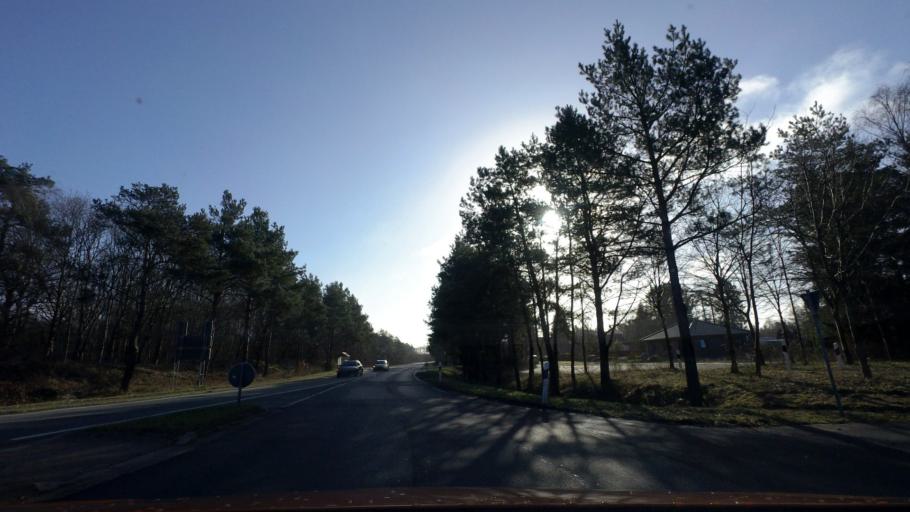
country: DE
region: Lower Saxony
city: Wardenburg
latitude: 53.0354
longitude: 8.2066
